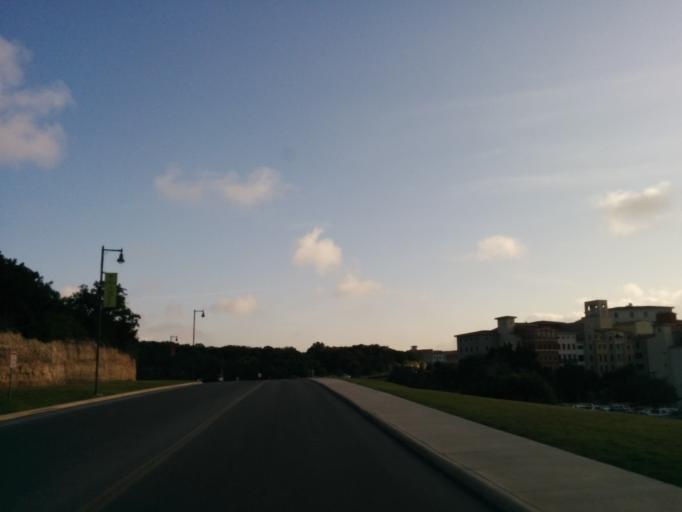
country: US
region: Texas
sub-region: Bexar County
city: Shavano Park
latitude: 29.6076
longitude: -98.6085
